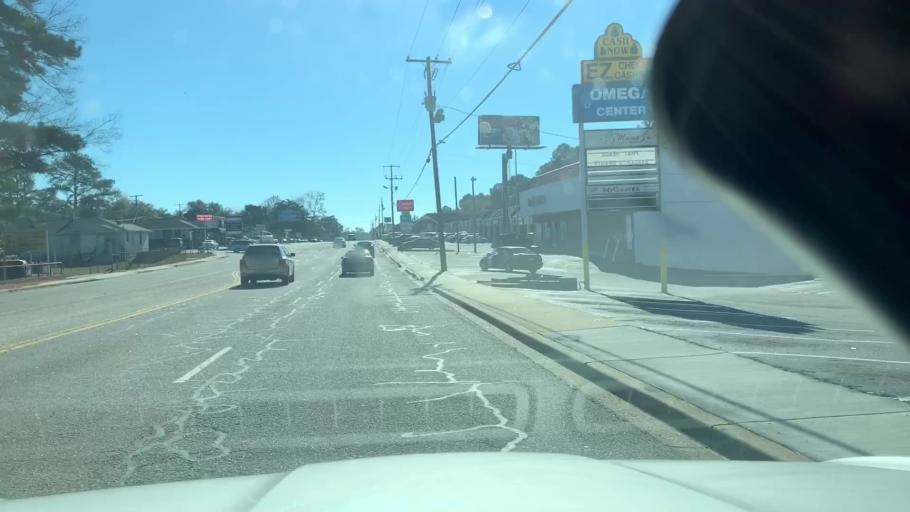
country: US
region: South Carolina
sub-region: Richland County
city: Woodfield
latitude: 34.0504
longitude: -80.9448
